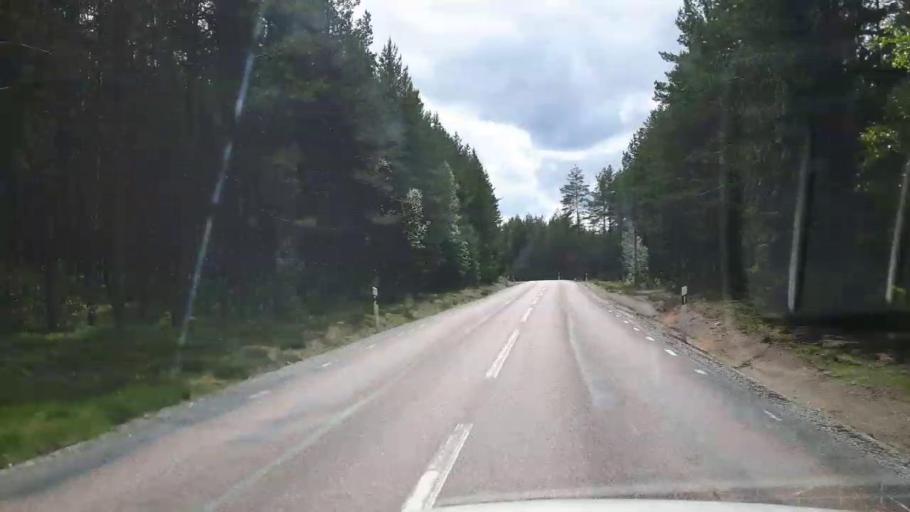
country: SE
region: Vaestmanland
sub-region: Fagersta Kommun
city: Fagersta
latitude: 59.9027
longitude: 15.8210
